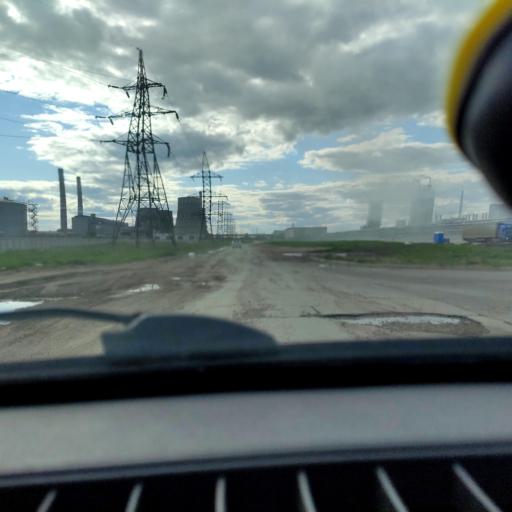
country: RU
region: Samara
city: Tol'yatti
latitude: 53.5468
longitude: 49.4718
